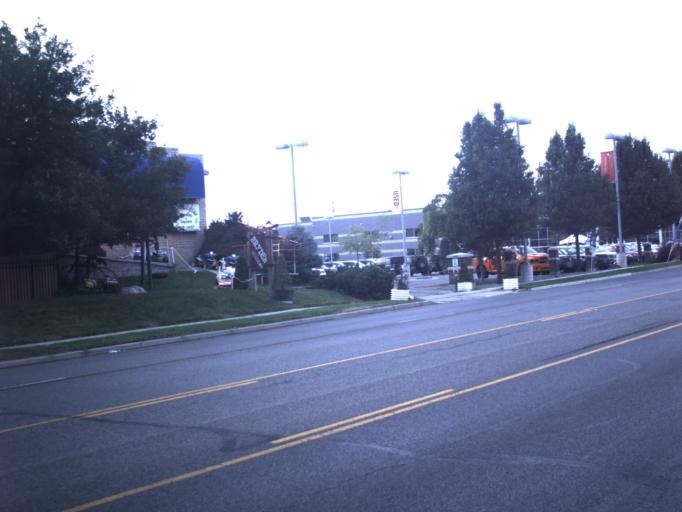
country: US
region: Utah
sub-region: Davis County
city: West Bountiful
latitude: 40.8956
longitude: -111.8921
